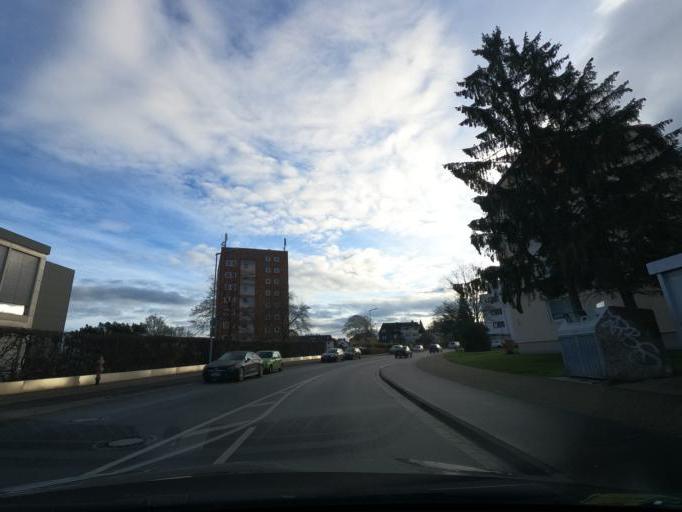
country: DE
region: Lower Saxony
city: Wolfenbuettel
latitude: 52.1665
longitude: 10.5479
